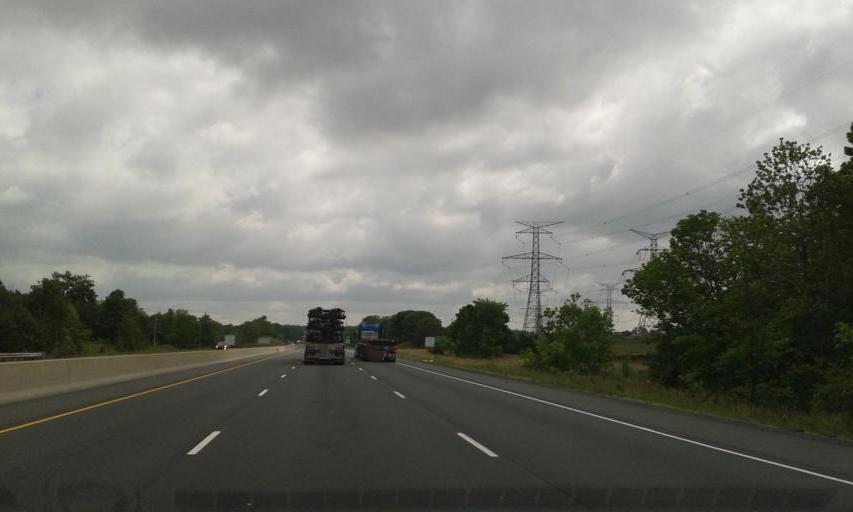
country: CA
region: Ontario
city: Cobourg
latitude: 43.9346
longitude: -78.4727
